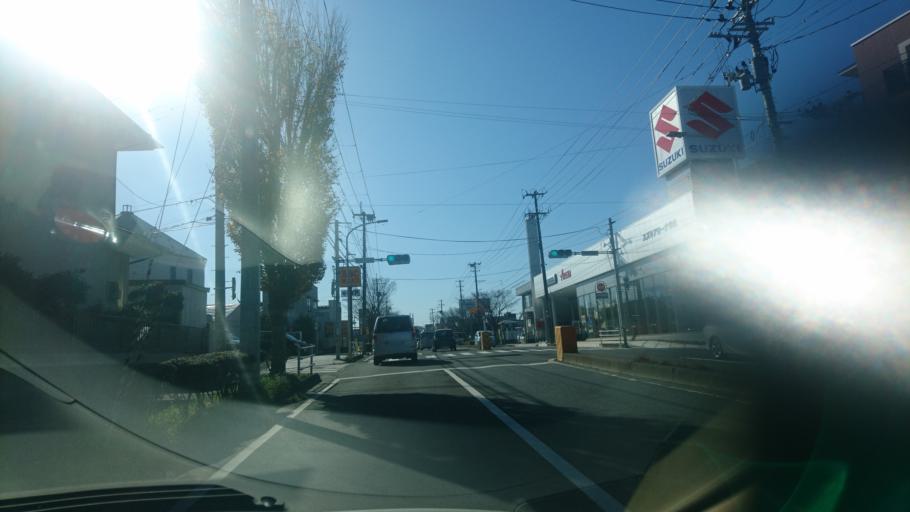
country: JP
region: Miyagi
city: Sendai-shi
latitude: 38.2895
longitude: 140.8204
